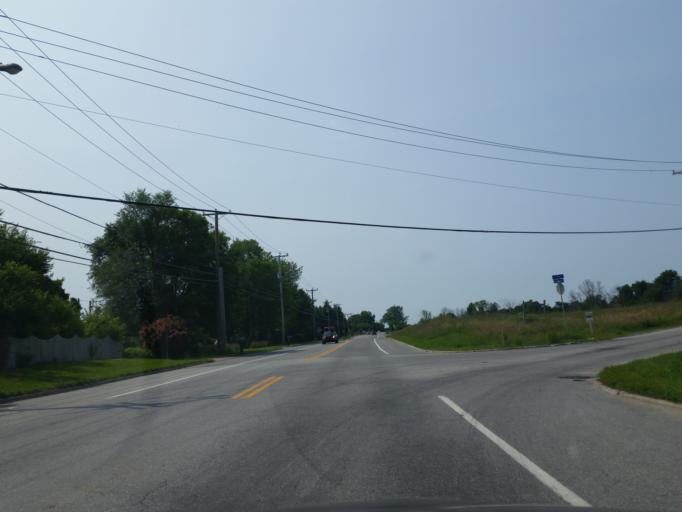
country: CA
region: Ontario
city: Bells Corners
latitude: 45.4142
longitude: -75.8775
